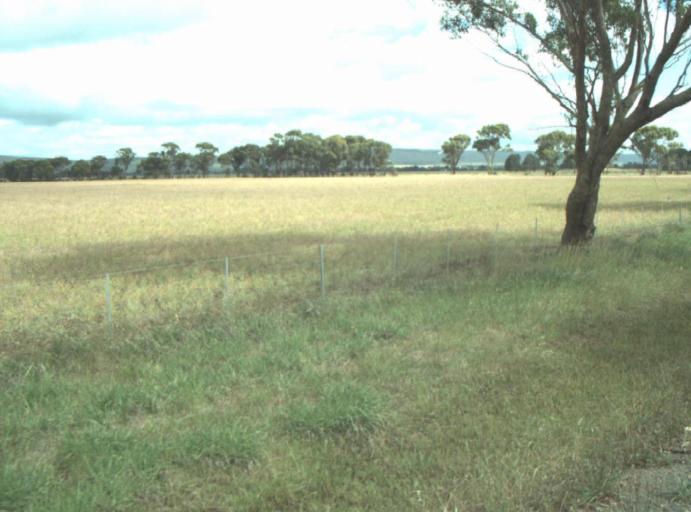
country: AU
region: Victoria
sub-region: Greater Geelong
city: Lara
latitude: -37.8719
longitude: 144.3501
